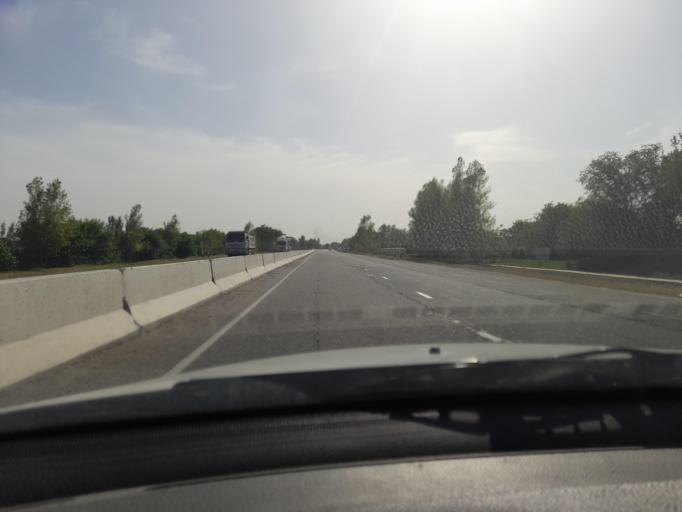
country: UZ
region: Samarqand
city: Ishtixon
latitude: 39.9417
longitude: 66.3966
